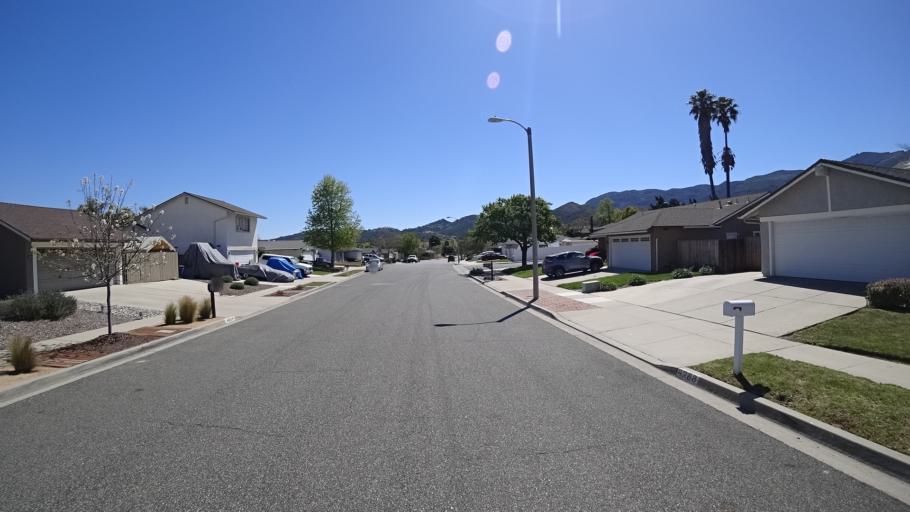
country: US
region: California
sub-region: Ventura County
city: Casa Conejo
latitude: 34.1579
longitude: -118.9660
